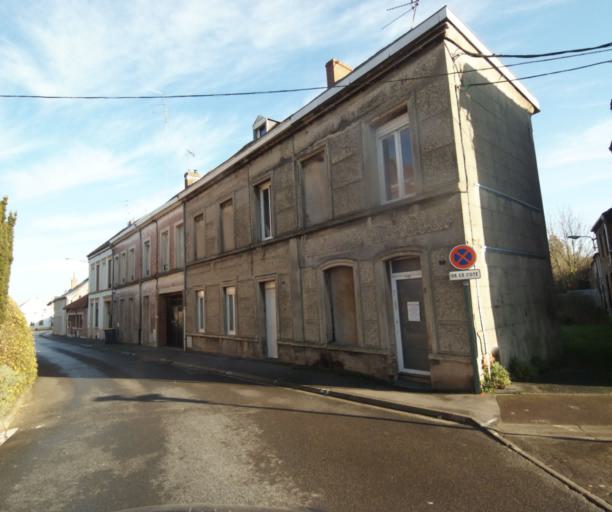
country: FR
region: Nord-Pas-de-Calais
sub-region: Departement du Nord
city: Aulnoy-lez-Valenciennes
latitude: 50.3302
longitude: 3.5295
